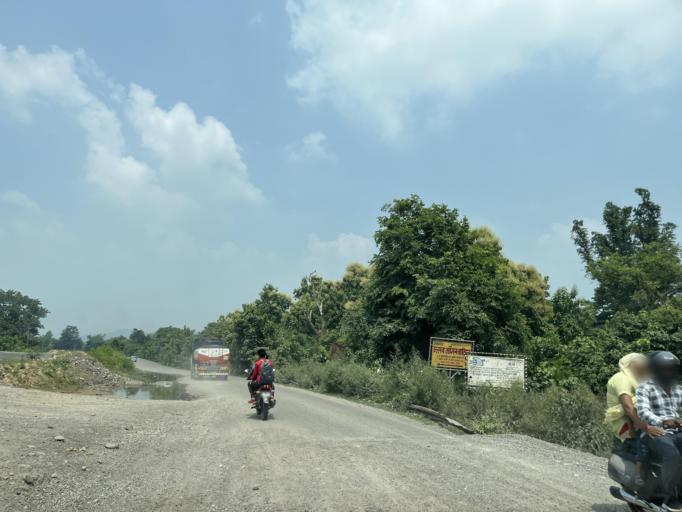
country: IN
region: Uttarakhand
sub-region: Haridwar
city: Haridwar
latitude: 29.8535
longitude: 78.1863
